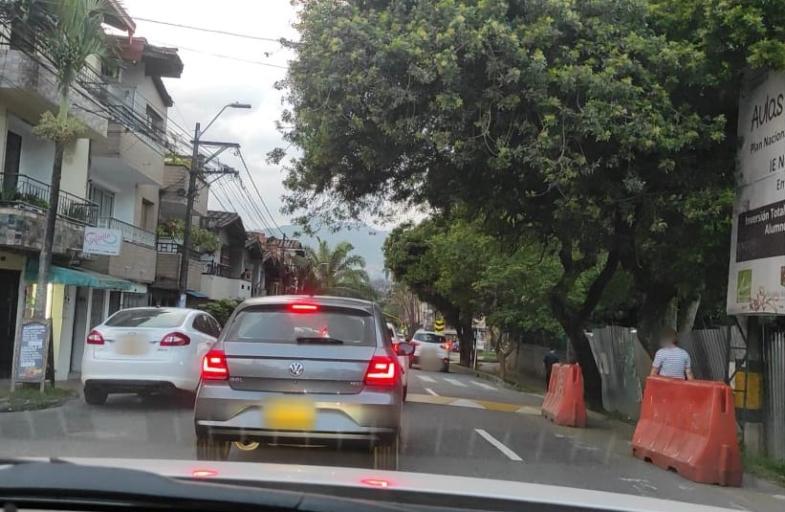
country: CO
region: Antioquia
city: Envigado
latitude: 6.1668
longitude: -75.5815
